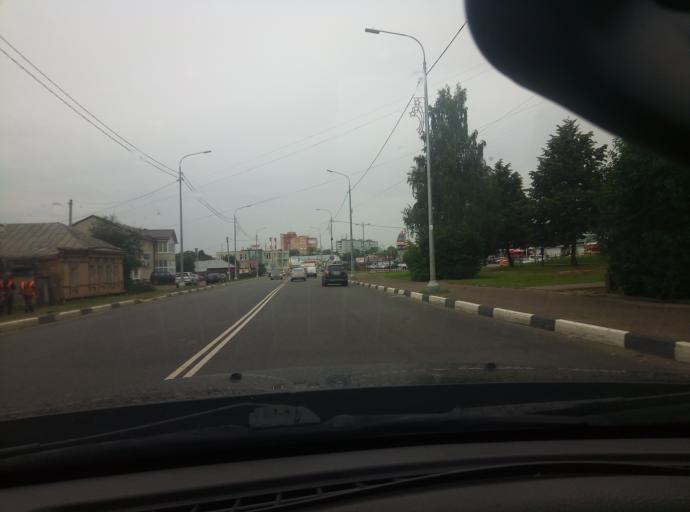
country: RU
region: Moskovskaya
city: Serpukhov
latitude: 54.9158
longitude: 37.4300
